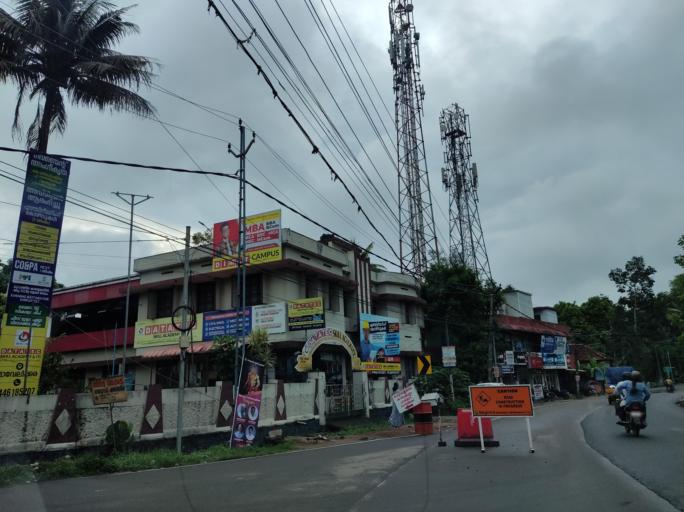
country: IN
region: Kerala
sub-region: Alappuzha
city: Mavelikara
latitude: 9.2493
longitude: 76.5339
